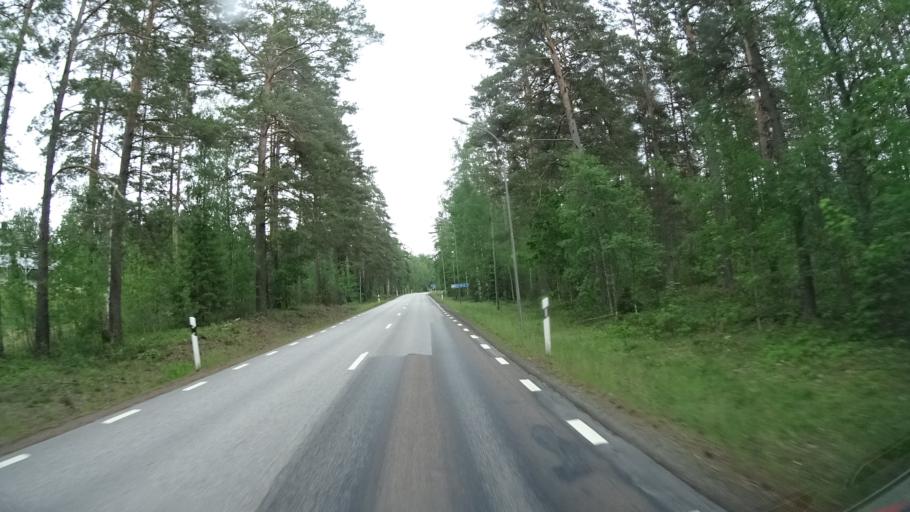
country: SE
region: Kalmar
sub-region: Hultsfreds Kommun
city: Hultsfred
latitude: 57.5344
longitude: 15.7668
